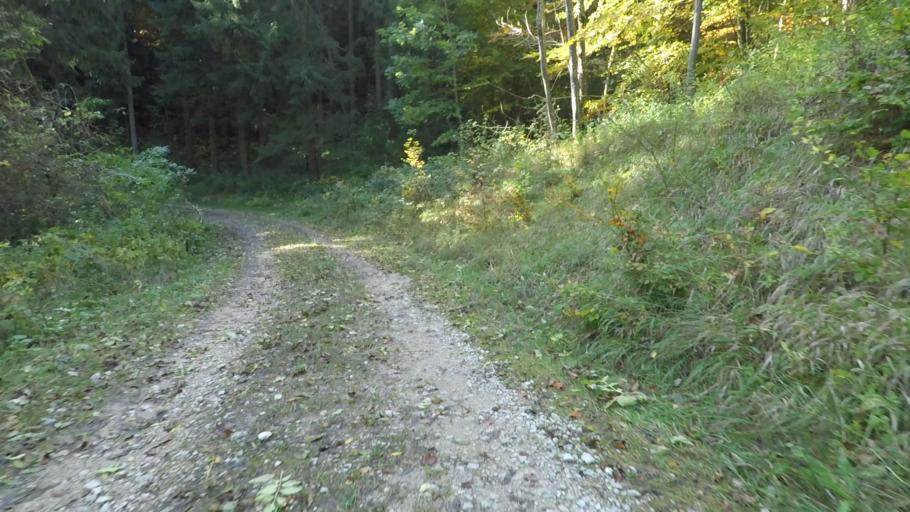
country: DE
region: Baden-Wuerttemberg
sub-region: Tuebingen Region
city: Pfullingen
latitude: 48.4318
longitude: 9.2273
